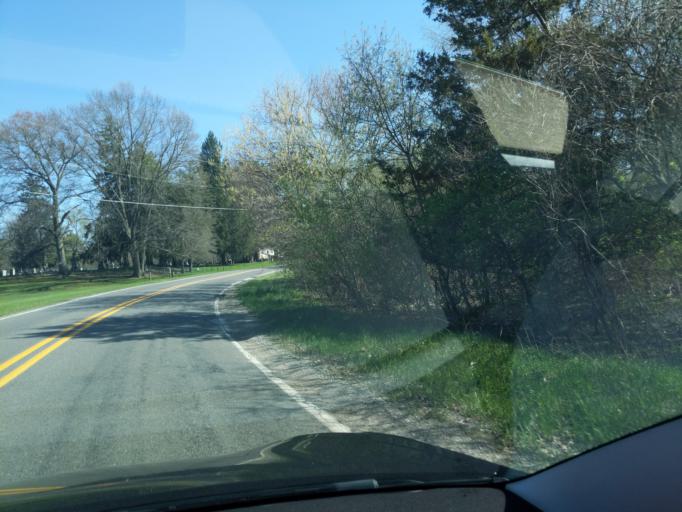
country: US
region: Michigan
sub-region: Ingham County
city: Stockbridge
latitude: 42.4420
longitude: -84.0972
